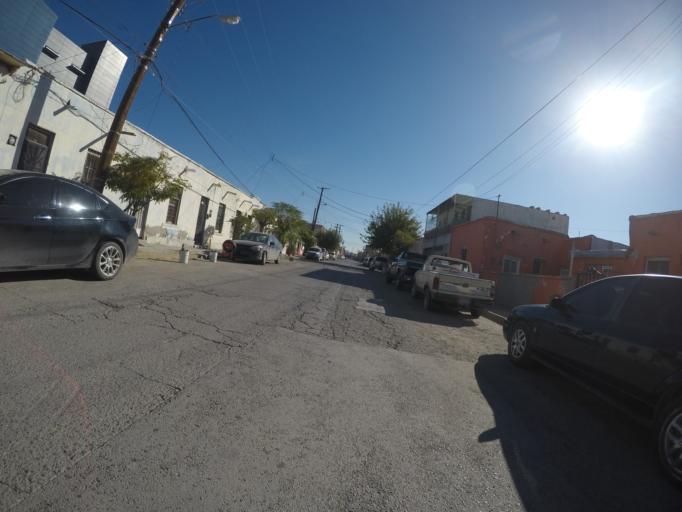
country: MX
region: Chihuahua
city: Ciudad Juarez
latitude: 31.7440
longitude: -106.4840
